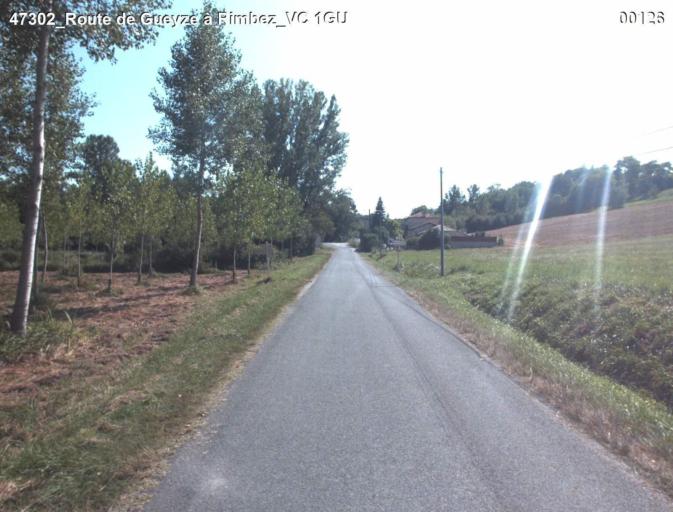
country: FR
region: Midi-Pyrenees
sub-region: Departement du Gers
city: Montreal
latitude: 44.0434
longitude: 0.1329
